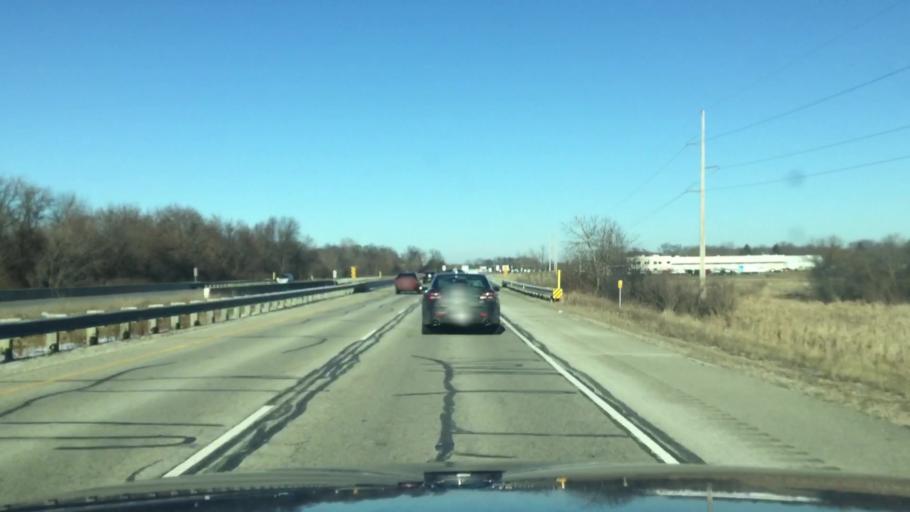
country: US
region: Wisconsin
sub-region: Racine County
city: Rochester
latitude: 42.7466
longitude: -88.2127
